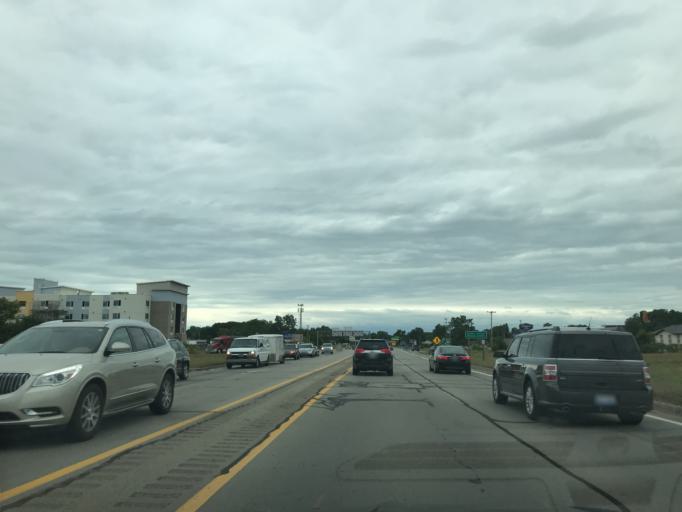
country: US
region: Michigan
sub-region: Jackson County
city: Jackson
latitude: 42.2730
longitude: -84.4278
